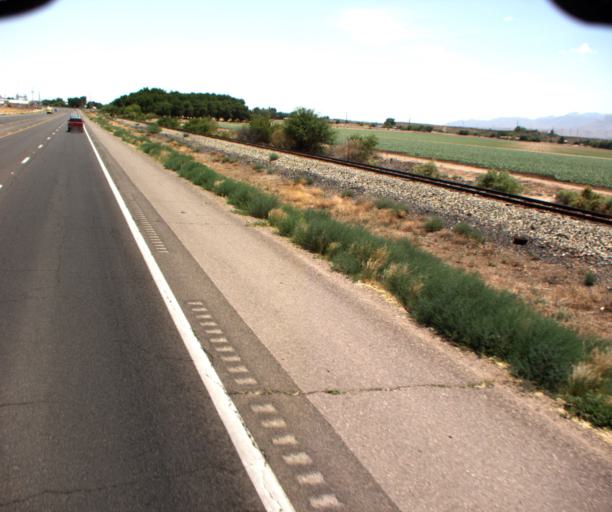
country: US
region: Arizona
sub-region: Graham County
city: Thatcher
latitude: 32.8567
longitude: -109.7818
